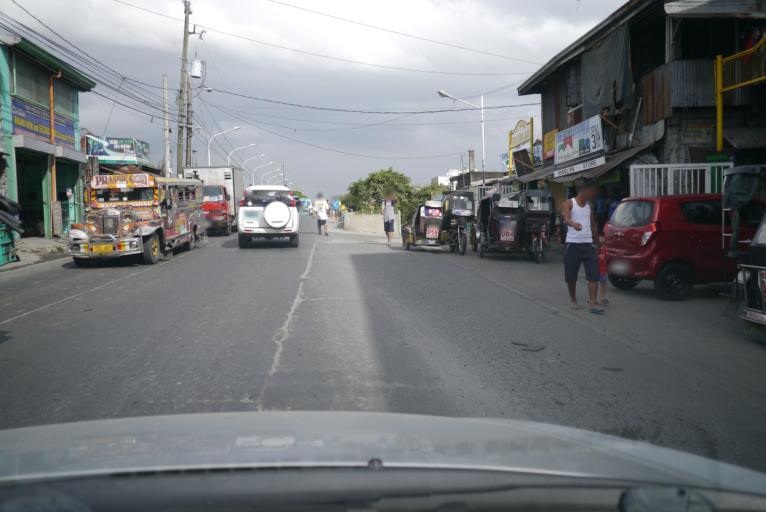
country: PH
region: Calabarzon
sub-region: Province of Rizal
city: Cainta
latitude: 14.5633
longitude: 121.1108
